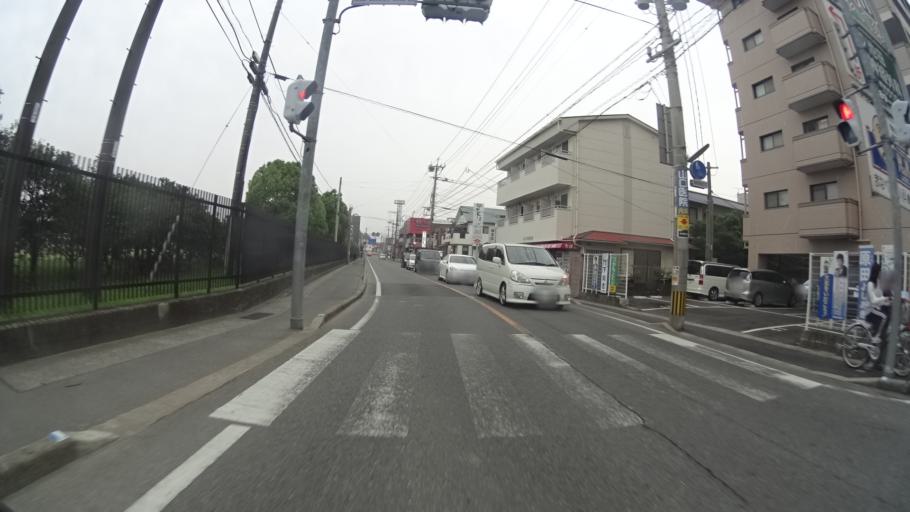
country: JP
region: Fukuoka
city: Onojo
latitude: 33.5420
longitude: 130.4541
